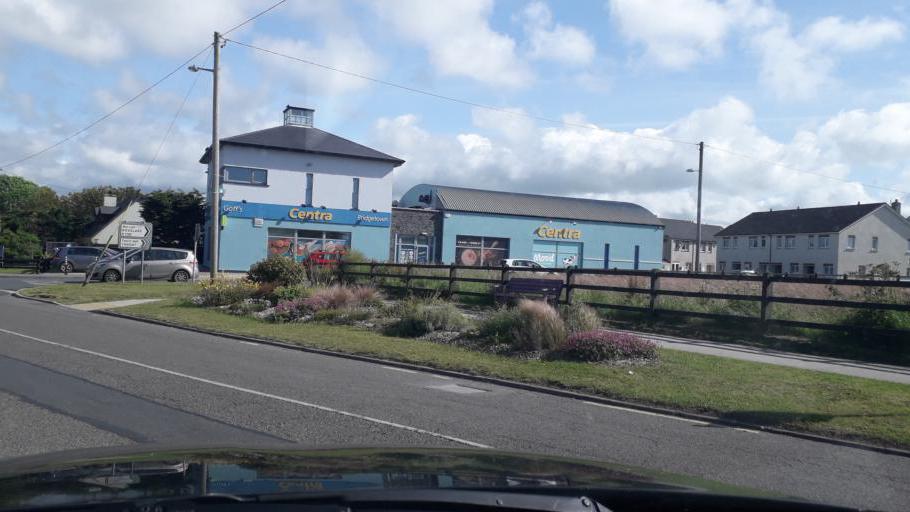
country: IE
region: Leinster
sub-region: Loch Garman
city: Loch Garman
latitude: 52.2297
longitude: -6.5518
